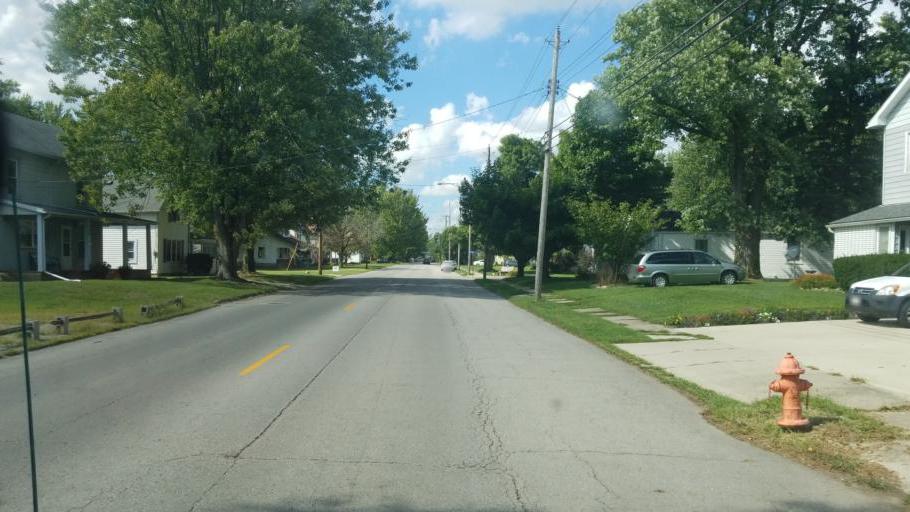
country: US
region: Ohio
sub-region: Union County
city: Richwood
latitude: 40.4196
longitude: -83.2934
